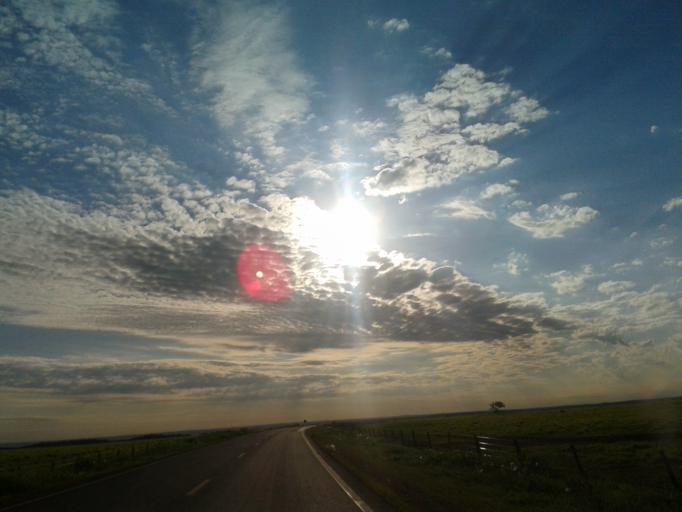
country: BR
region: Minas Gerais
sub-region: Capinopolis
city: Capinopolis
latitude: -18.6887
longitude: -49.5093
